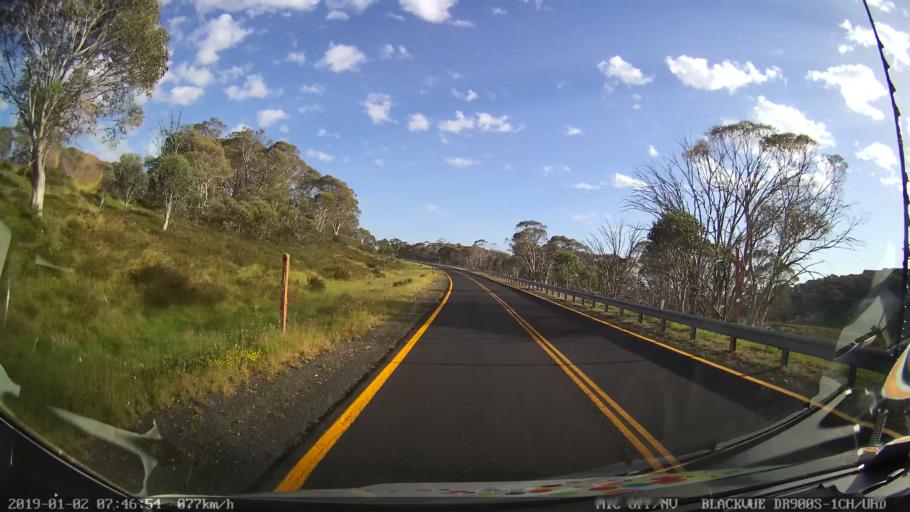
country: AU
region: New South Wales
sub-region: Tumut Shire
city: Tumut
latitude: -35.7707
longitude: 148.5210
